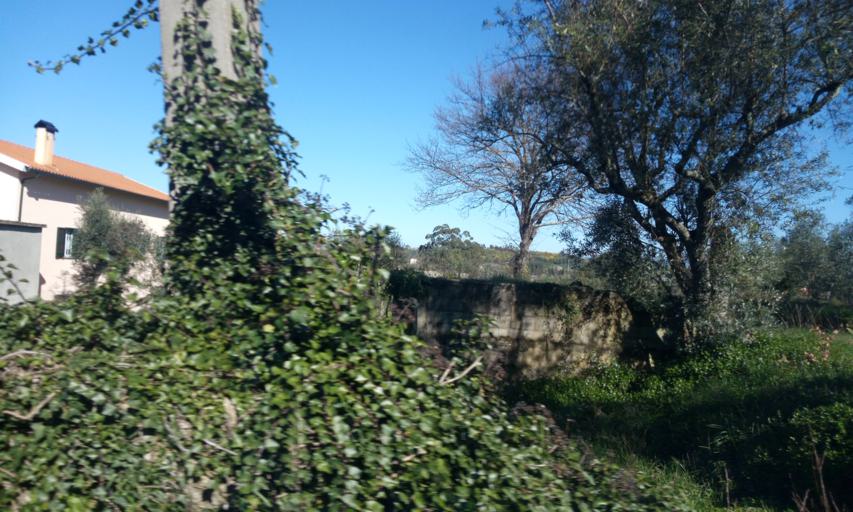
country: PT
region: Guarda
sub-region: Manteigas
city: Manteigas
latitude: 40.5116
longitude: -7.6093
